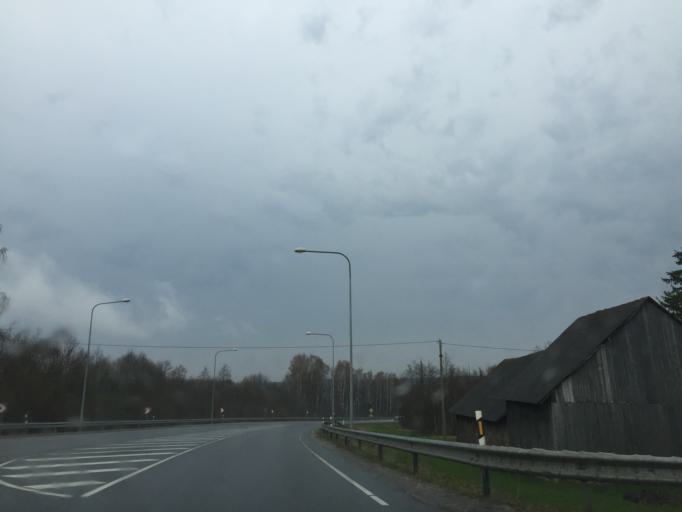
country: EE
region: Tartu
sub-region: UElenurme vald
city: Ulenurme
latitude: 58.2481
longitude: 26.6788
